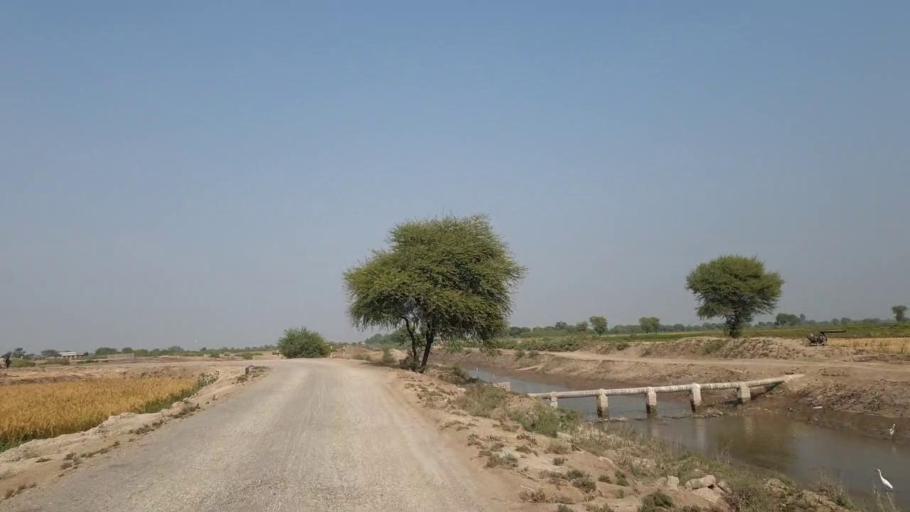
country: PK
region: Sindh
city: Matli
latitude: 24.9519
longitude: 68.5278
